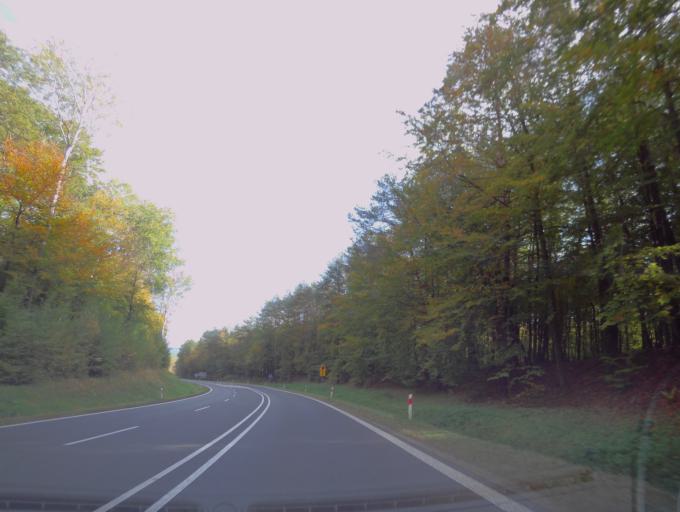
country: PL
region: Lublin Voivodeship
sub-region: Powiat bilgorajski
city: Turobin
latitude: 50.8105
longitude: 22.6933
